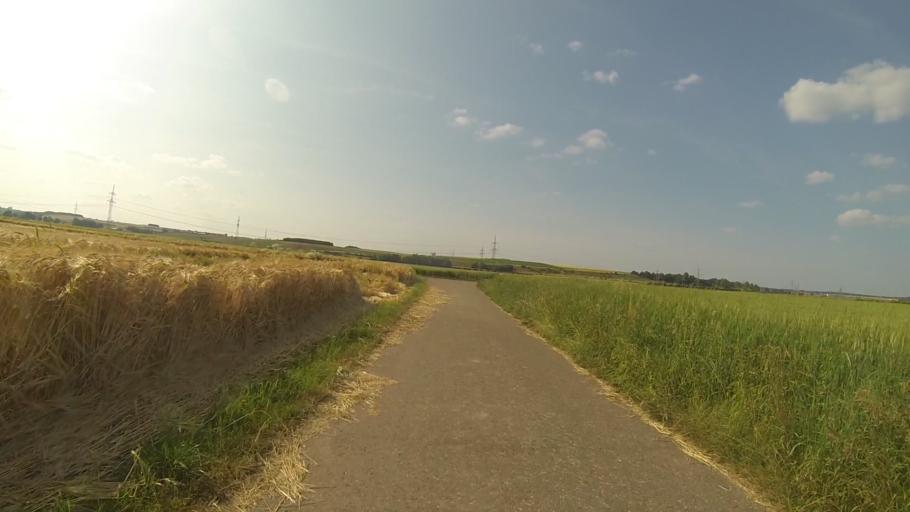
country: DE
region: Baden-Wuerttemberg
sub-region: Regierungsbezirk Stuttgart
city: Niederstotzingen
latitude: 48.5126
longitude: 10.2202
